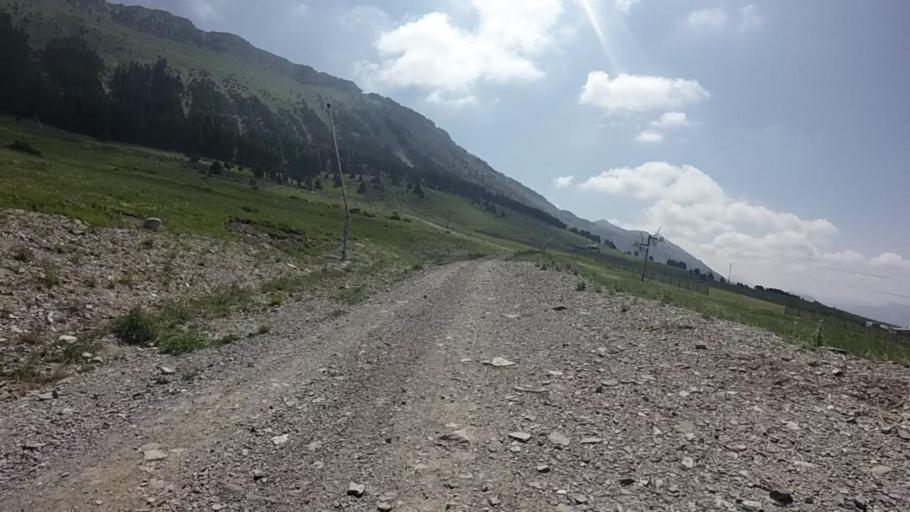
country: FR
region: Provence-Alpes-Cote d'Azur
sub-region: Departement des Alpes-de-Haute-Provence
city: Seyne-les-Alpes
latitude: 44.3987
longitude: 6.3748
